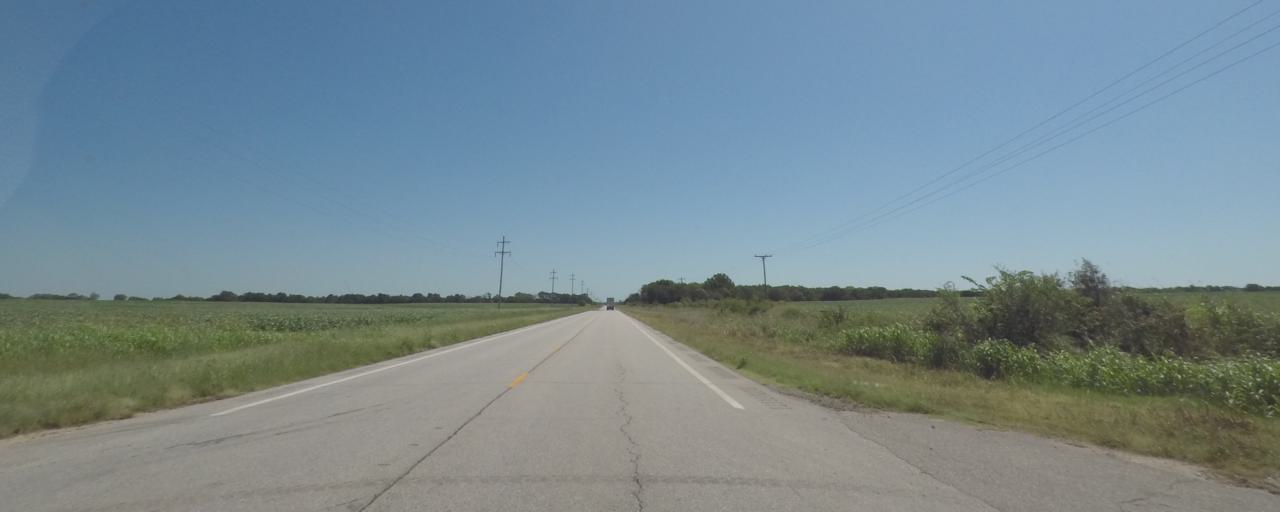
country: US
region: Kansas
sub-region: Sumner County
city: Belle Plaine
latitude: 37.3913
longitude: -97.3671
